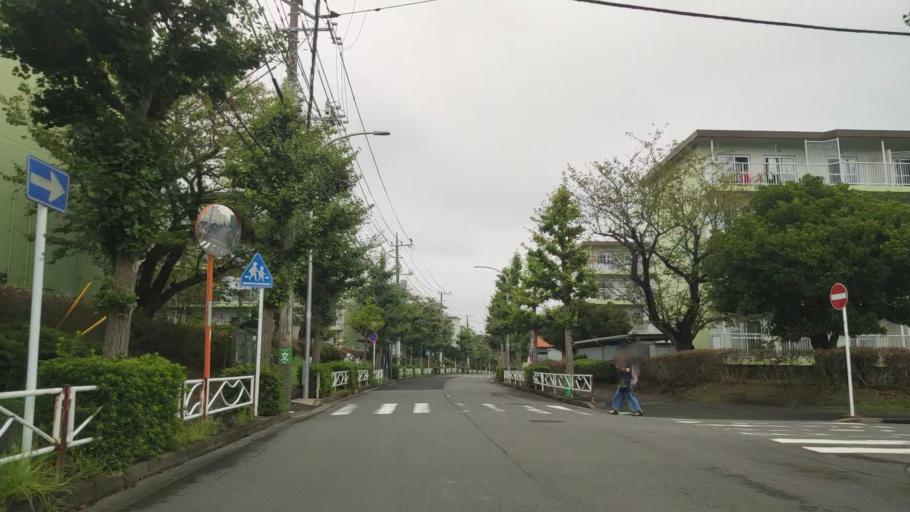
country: JP
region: Kanagawa
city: Zushi
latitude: 35.3663
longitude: 139.6090
